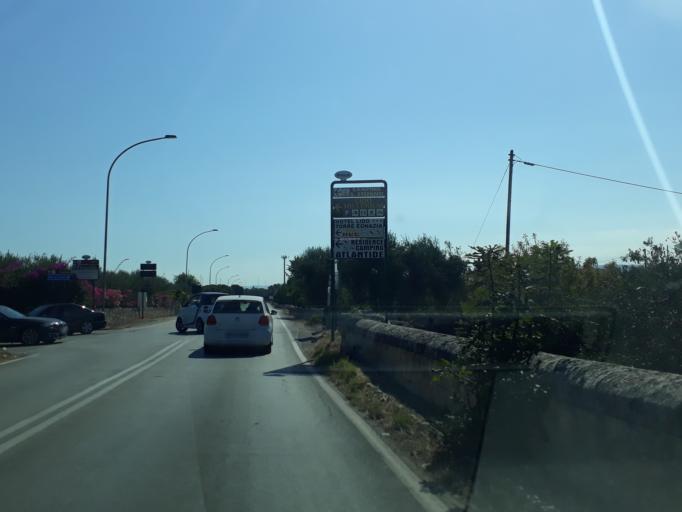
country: IT
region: Apulia
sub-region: Provincia di Bari
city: Monopoli
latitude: 40.9277
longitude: 17.3134
